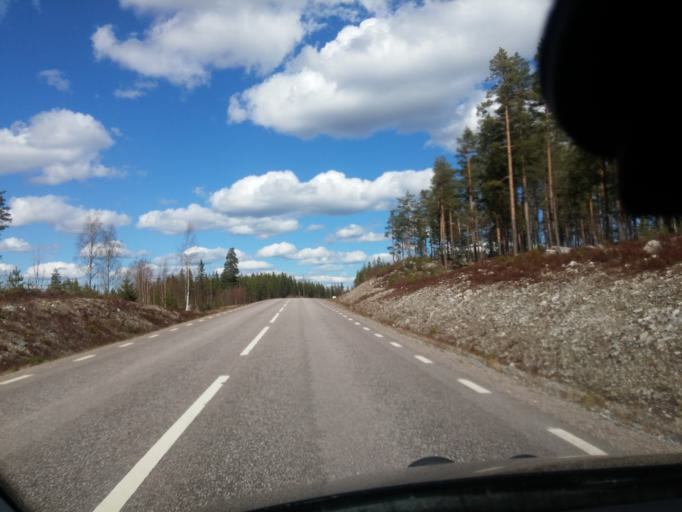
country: SE
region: Gaevleborg
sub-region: Ovanakers Kommun
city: Edsbyn
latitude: 61.2433
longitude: 15.8834
